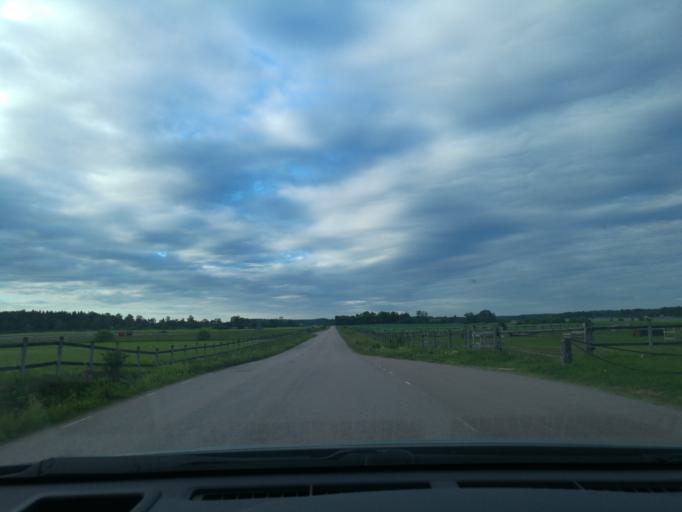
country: SE
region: Vaestmanland
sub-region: Hallstahammars Kommun
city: Kolback
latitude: 59.5304
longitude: 16.2907
